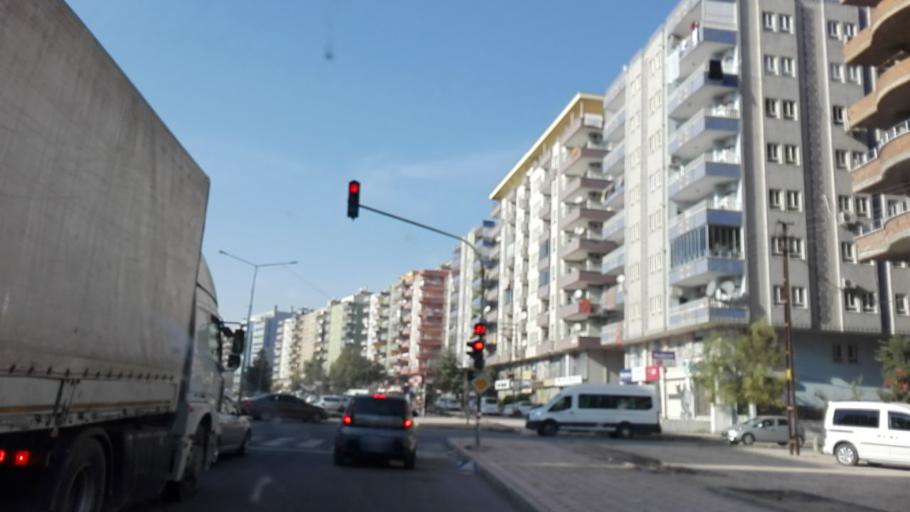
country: TR
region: Batman
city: Demiryol
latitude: 37.9003
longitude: 41.1459
